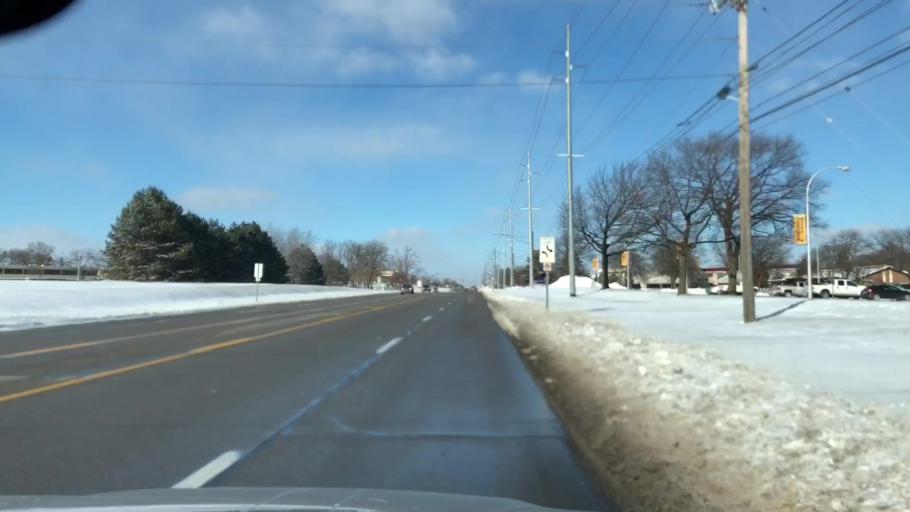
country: US
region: Michigan
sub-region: Wayne County
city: Northville
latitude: 42.4180
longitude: -83.4326
